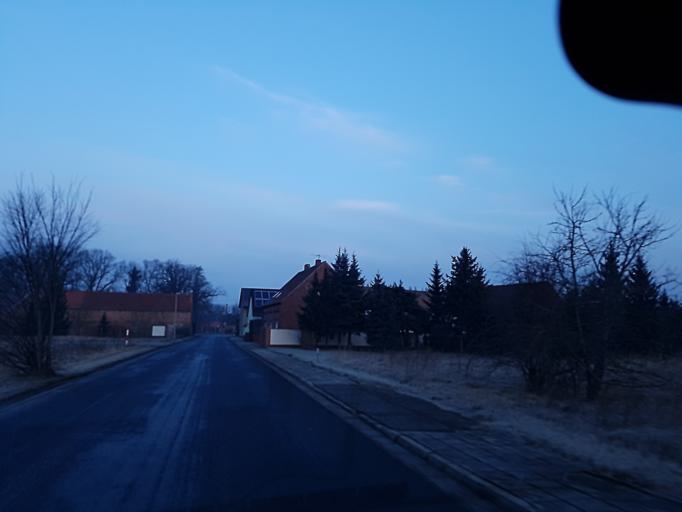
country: DE
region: Saxony-Anhalt
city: Holzdorf
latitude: 51.7689
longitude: 13.0857
